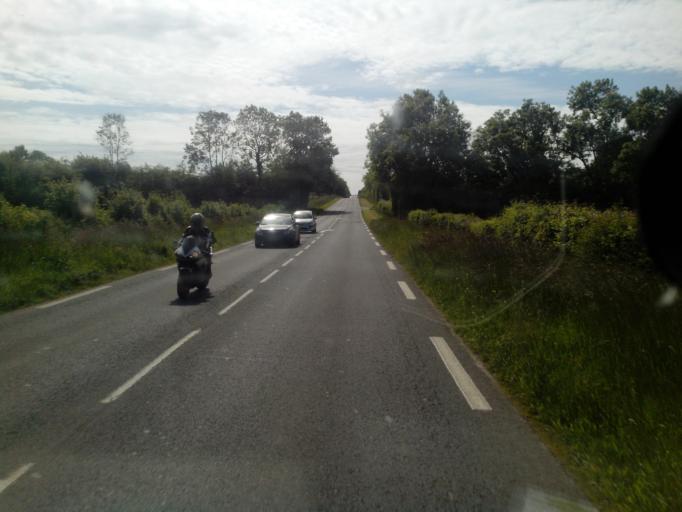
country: FR
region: Lower Normandy
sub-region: Departement du Calvados
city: Touques
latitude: 49.2572
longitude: 0.0765
